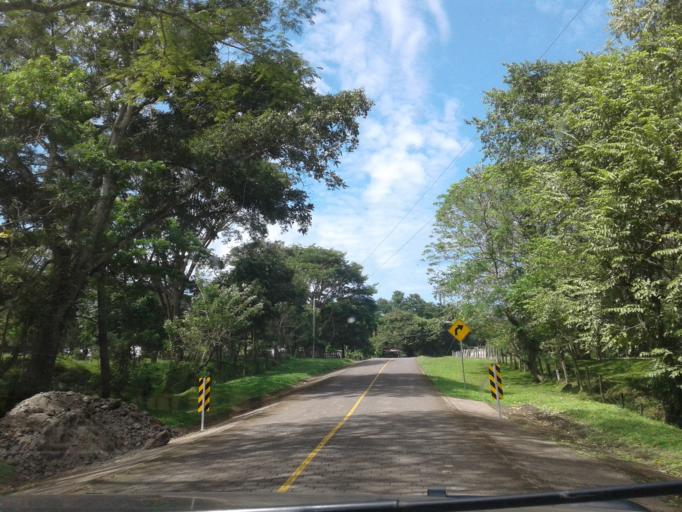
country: NI
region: Rivas
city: Cardenas
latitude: 11.1766
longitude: -85.4875
